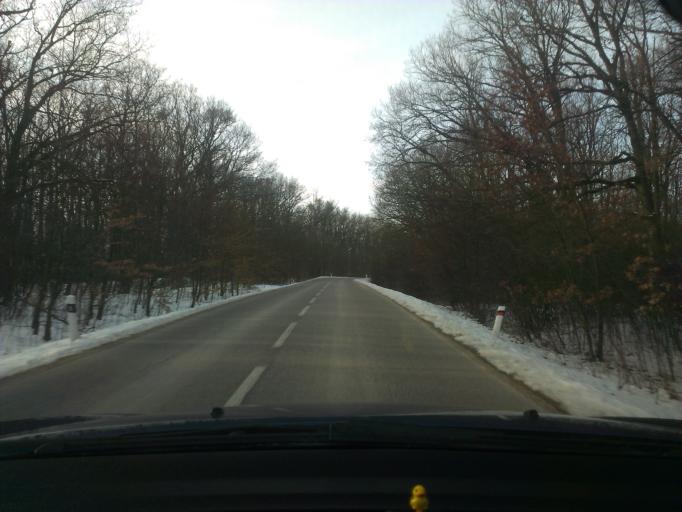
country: SK
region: Nitriansky
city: Stara Tura
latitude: 48.7254
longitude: 17.6750
